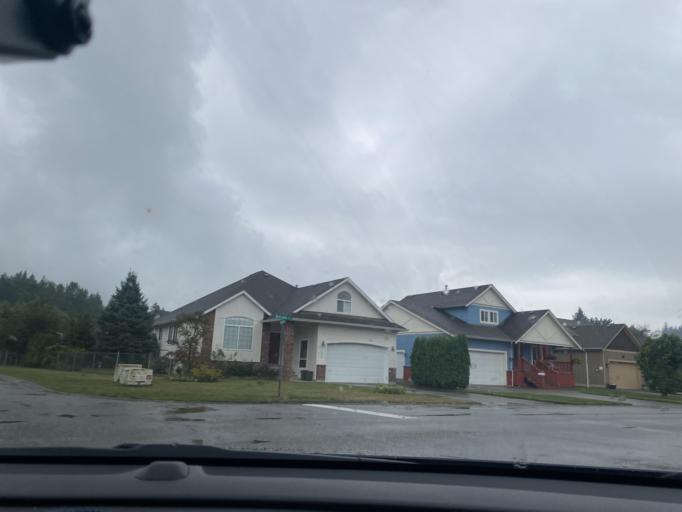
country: CA
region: British Columbia
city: Agassiz
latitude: 49.2971
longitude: -121.7801
